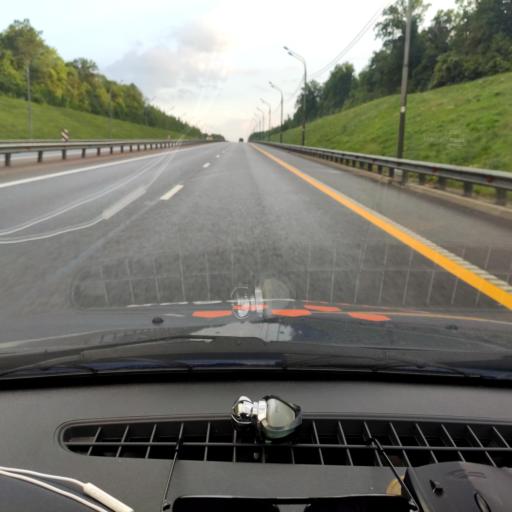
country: RU
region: Lipetsk
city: Zadonsk
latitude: 52.4089
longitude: 38.8515
